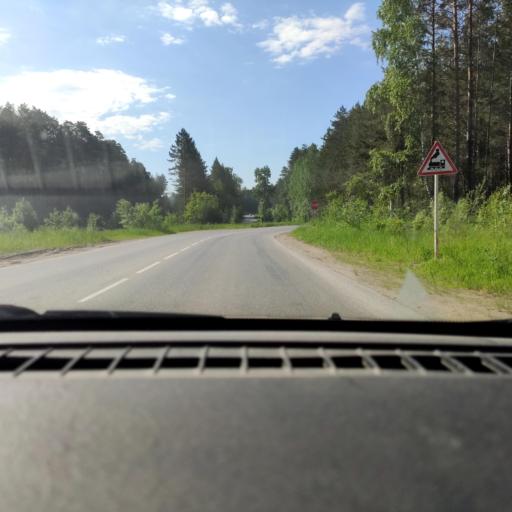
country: RU
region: Perm
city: Overyata
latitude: 57.9985
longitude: 55.8805
